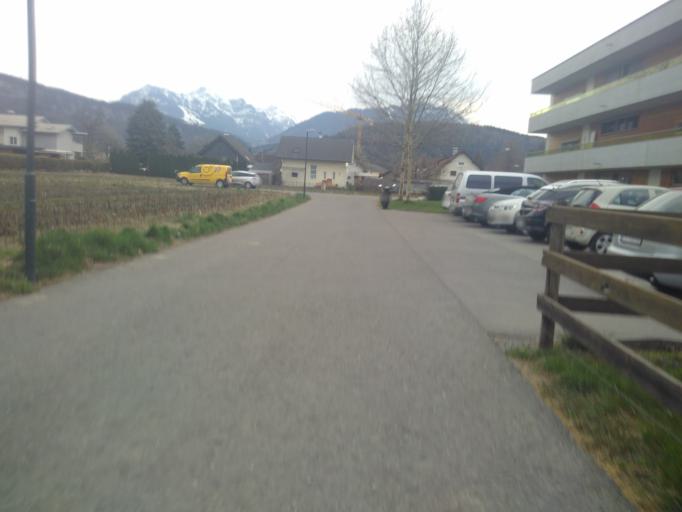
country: AT
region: Vorarlberg
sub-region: Politischer Bezirk Feldkirch
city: Rankweil
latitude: 47.2689
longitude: 9.6132
